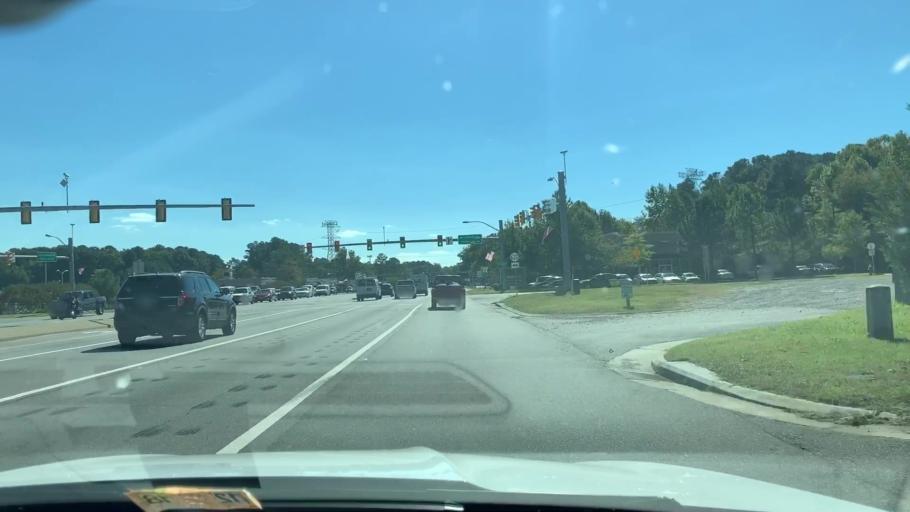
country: US
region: Virginia
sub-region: York County
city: Yorktown
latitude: 37.1481
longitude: -76.4594
